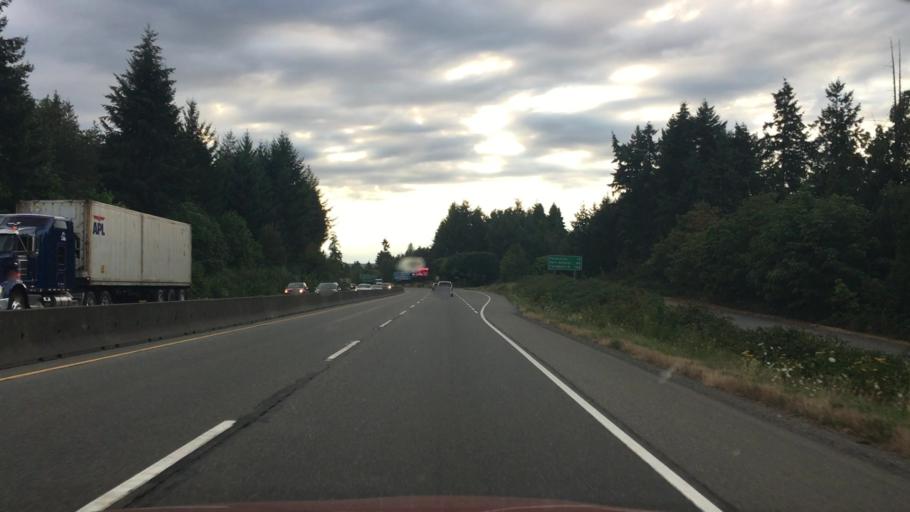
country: CA
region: British Columbia
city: Nanaimo
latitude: 49.2516
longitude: -124.1090
